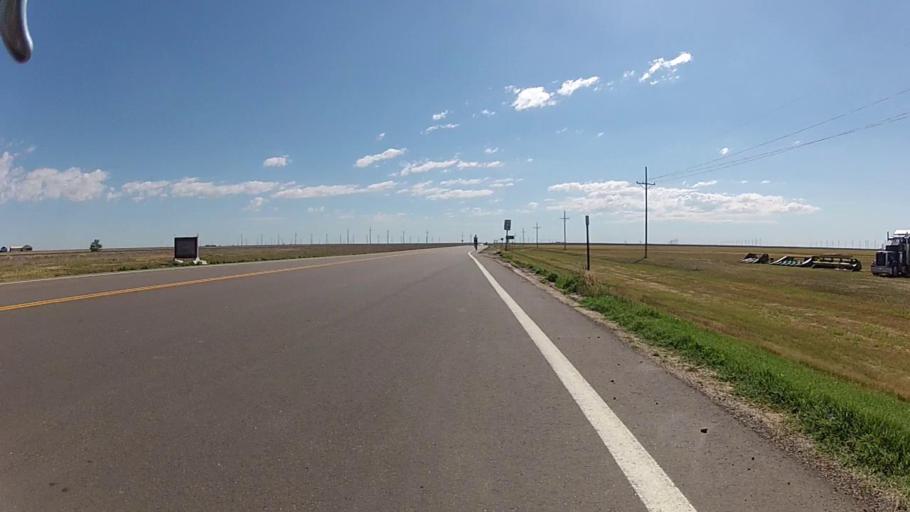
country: US
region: Kansas
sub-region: Gray County
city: Cimarron
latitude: 37.6016
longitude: -100.4334
